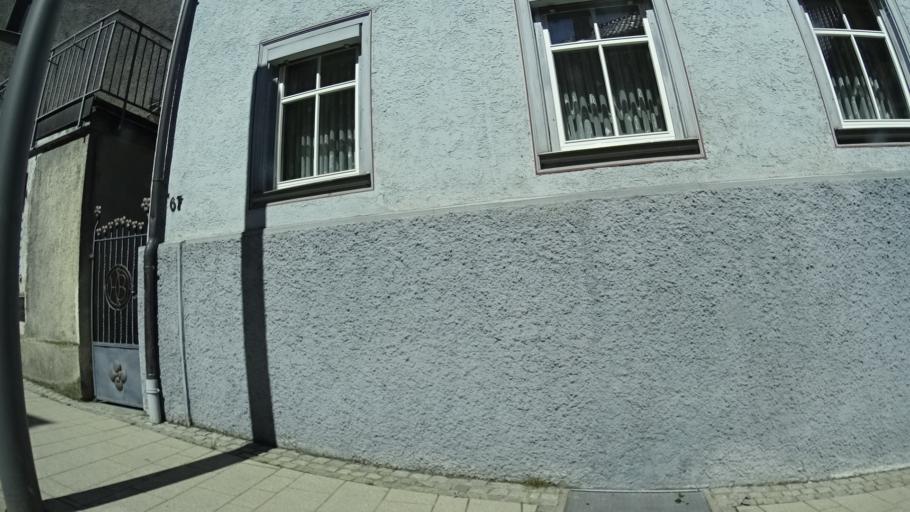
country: DE
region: Baden-Wuerttemberg
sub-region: Freiburg Region
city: Rottweil
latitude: 48.1684
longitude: 8.6297
